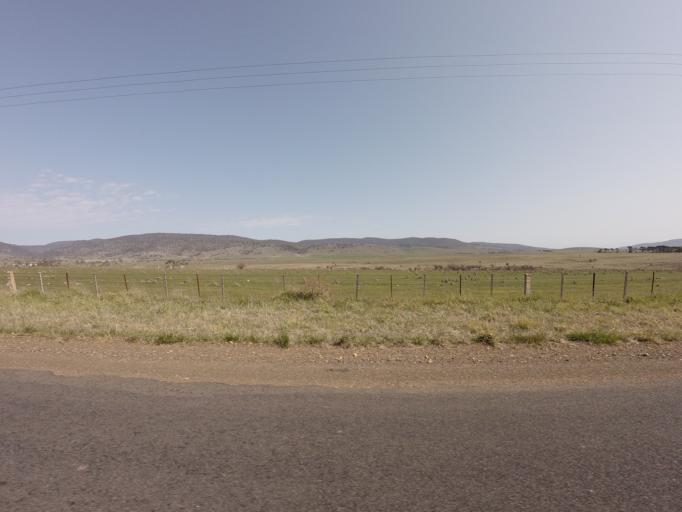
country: AU
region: Tasmania
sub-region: Northern Midlands
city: Evandale
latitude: -41.8212
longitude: 147.7578
